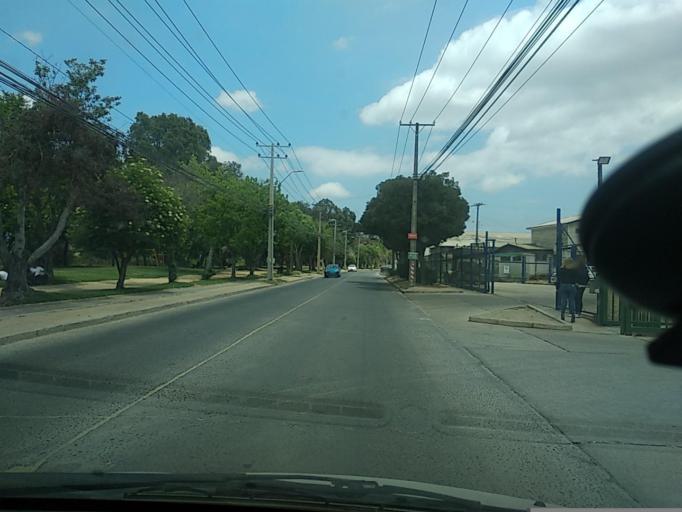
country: CL
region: Valparaiso
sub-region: Provincia de Marga Marga
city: Quilpue
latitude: -33.0411
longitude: -71.4137
